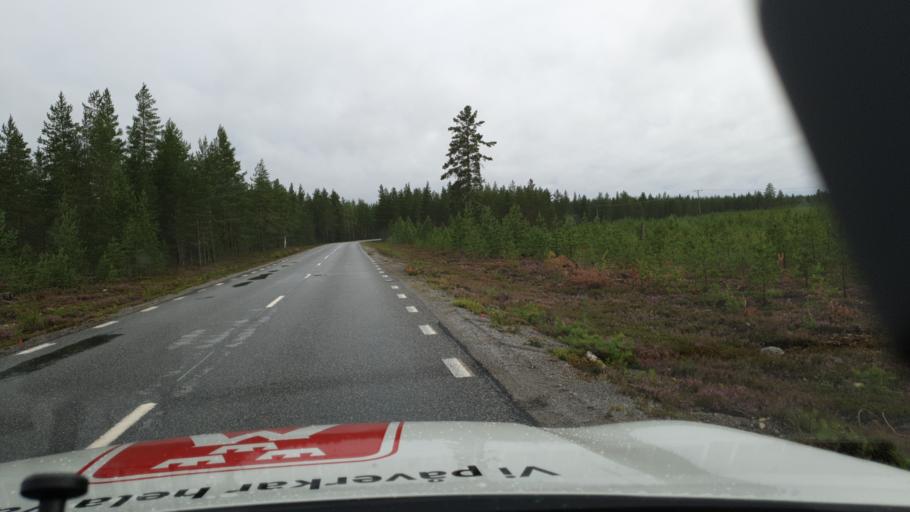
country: SE
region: Vaesterbotten
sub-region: Umea Kommun
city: Saevar
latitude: 63.9735
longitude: 20.5060
